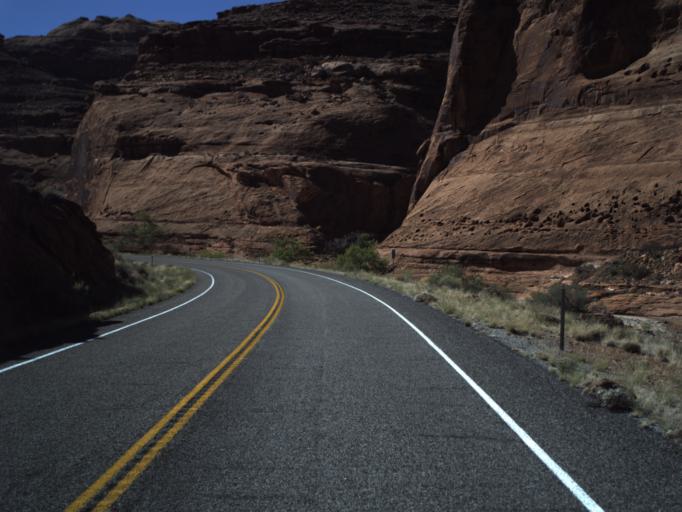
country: US
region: Utah
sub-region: San Juan County
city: Blanding
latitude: 37.9664
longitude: -110.4922
